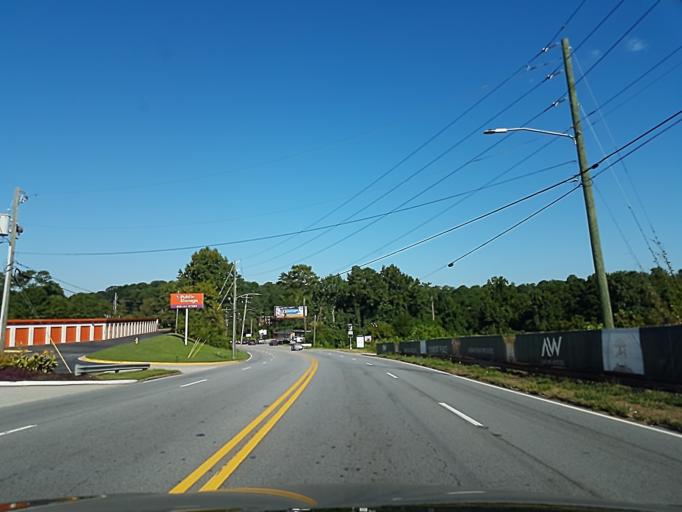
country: US
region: Georgia
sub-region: DeKalb County
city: North Druid Hills
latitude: 33.8119
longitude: -84.2938
